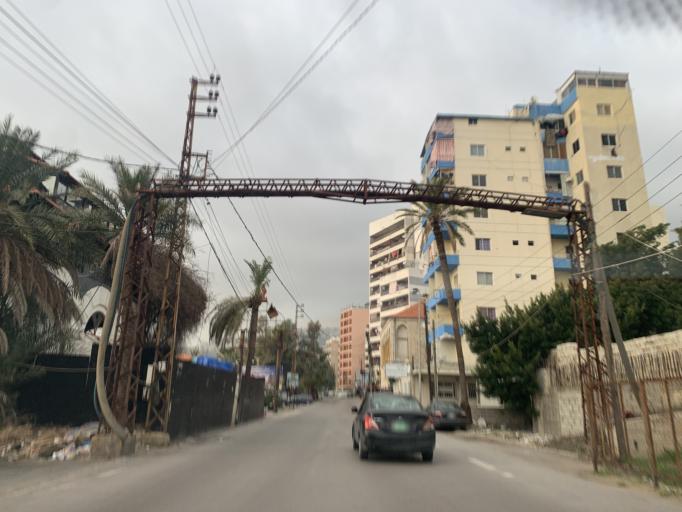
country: LB
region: Mont-Liban
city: Djounie
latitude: 34.0018
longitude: 35.6447
